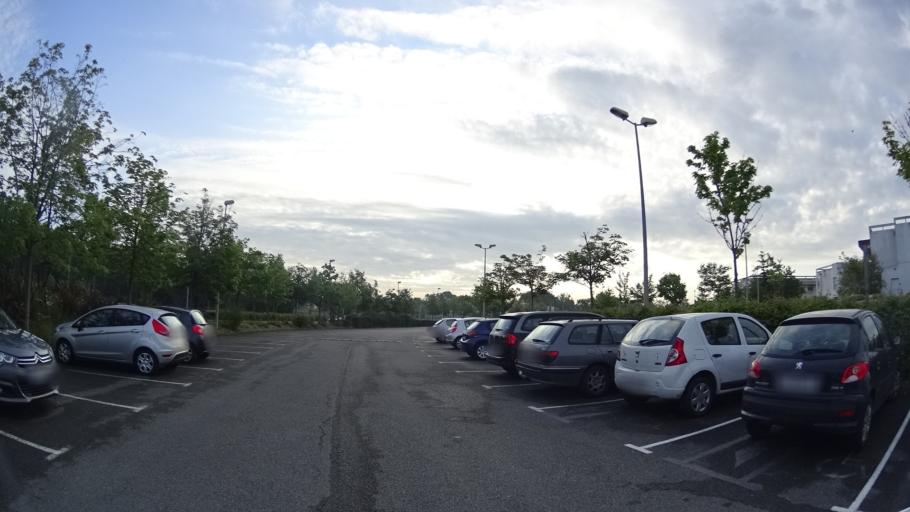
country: FR
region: Brittany
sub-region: Departement du Morbihan
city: Vannes
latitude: 47.6459
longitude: -2.7466
